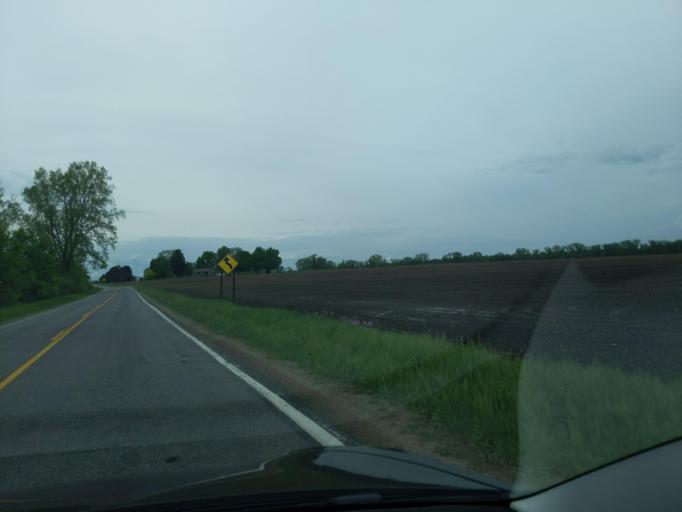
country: US
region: Michigan
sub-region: Ingham County
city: Mason
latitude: 42.5414
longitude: -84.4231
